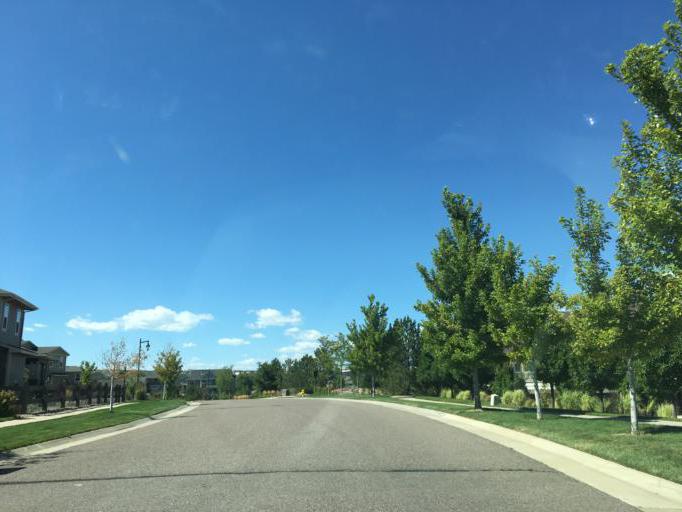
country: US
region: Colorado
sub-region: Douglas County
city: Parker
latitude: 39.5968
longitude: -104.6710
